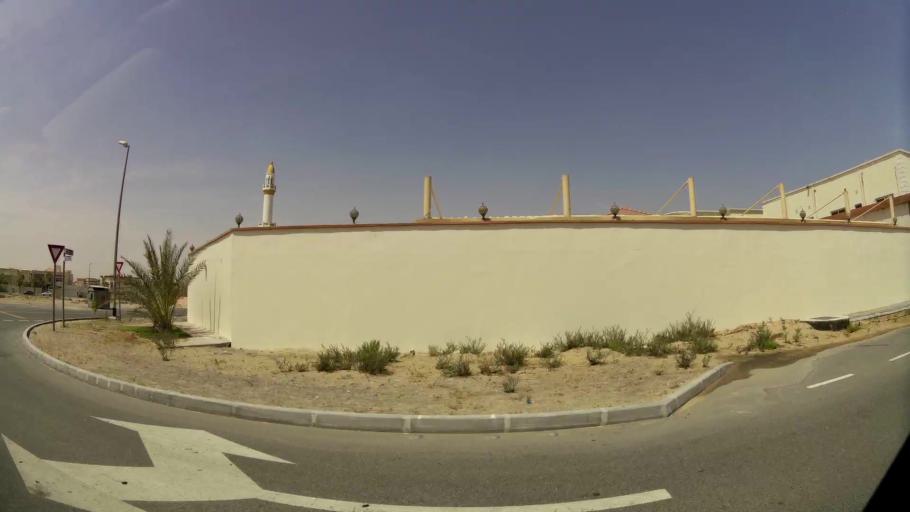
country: AE
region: Ash Shariqah
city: Sharjah
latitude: 25.1893
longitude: 55.4237
